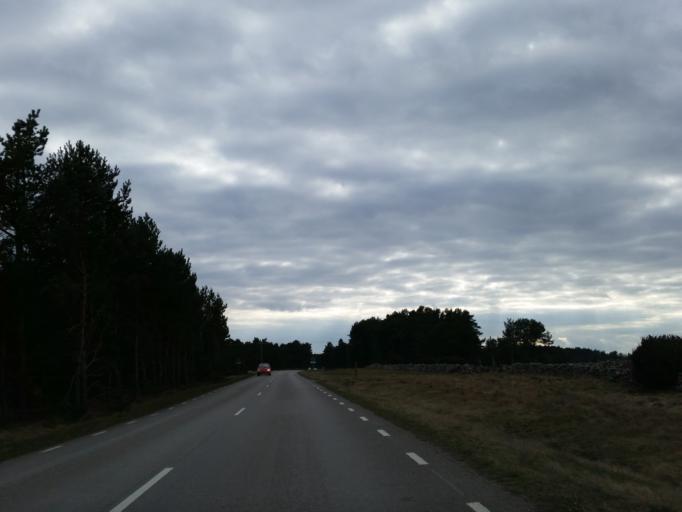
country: SE
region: Kalmar
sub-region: Morbylanga Kommun
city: Sodra Sandby
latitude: 56.5900
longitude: 16.6309
